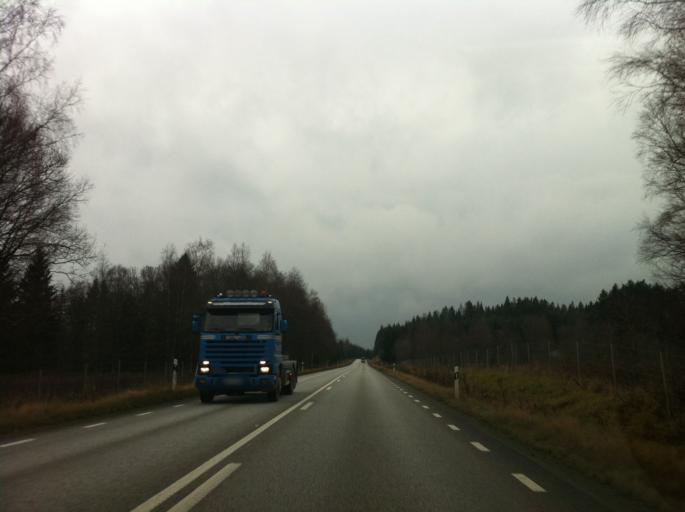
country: SE
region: Joenkoeping
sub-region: Savsjo Kommun
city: Saevsjoe
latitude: 57.3957
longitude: 14.6771
